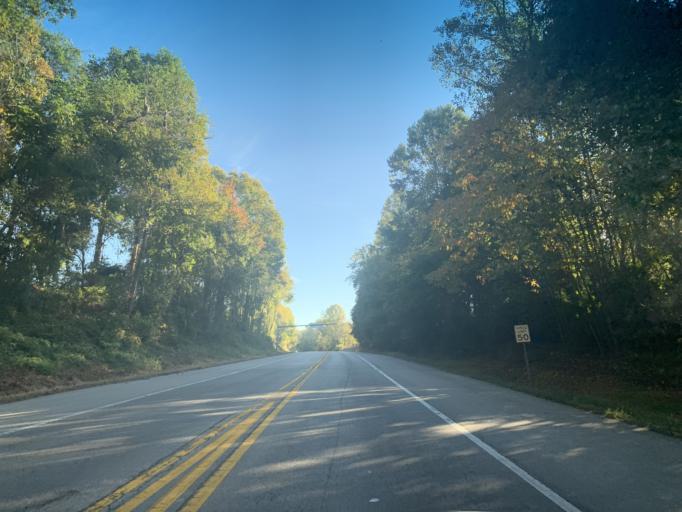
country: US
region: Maryland
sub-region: Cecil County
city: Rising Sun
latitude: 39.7092
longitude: -76.0635
